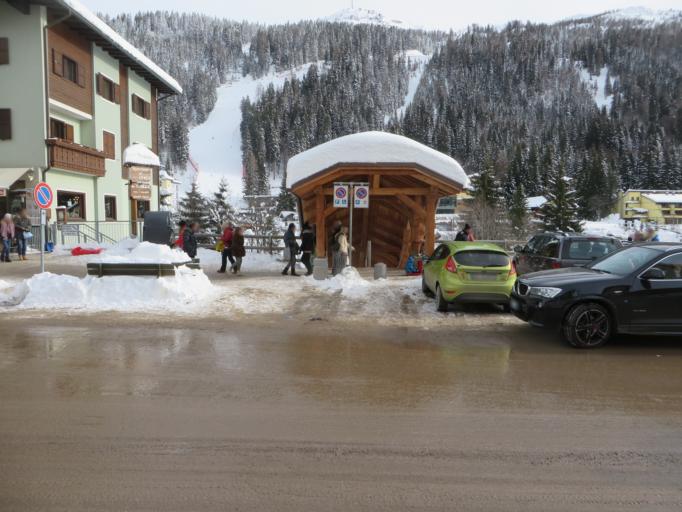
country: IT
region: Trentino-Alto Adige
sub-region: Provincia di Trento
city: Carisolo
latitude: 46.2284
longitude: 10.8264
